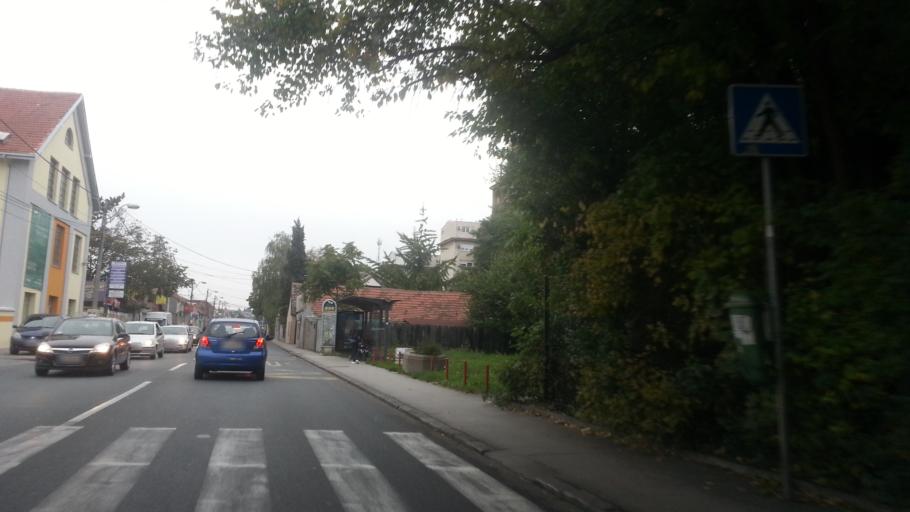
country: RS
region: Central Serbia
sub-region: Belgrade
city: Zemun
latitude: 44.8313
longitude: 20.3999
